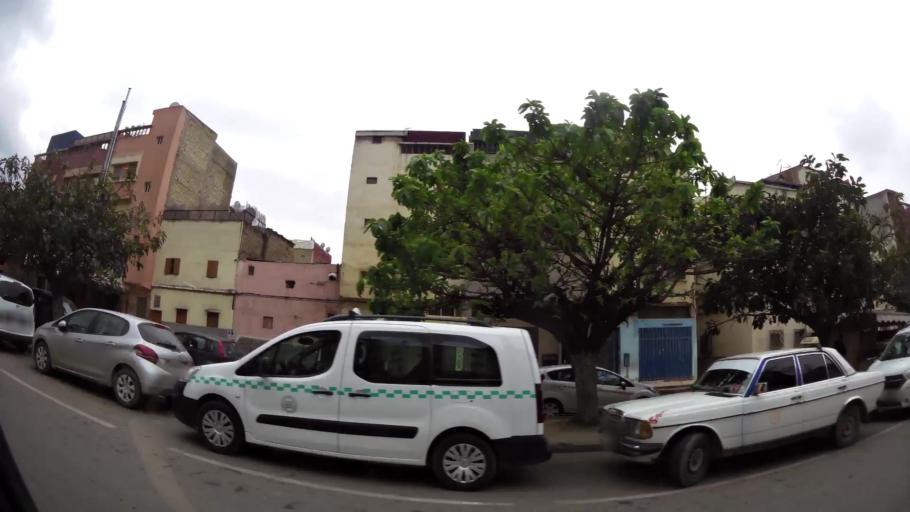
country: MA
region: Grand Casablanca
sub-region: Mediouna
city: Tit Mellil
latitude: 33.5599
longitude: -7.5510
